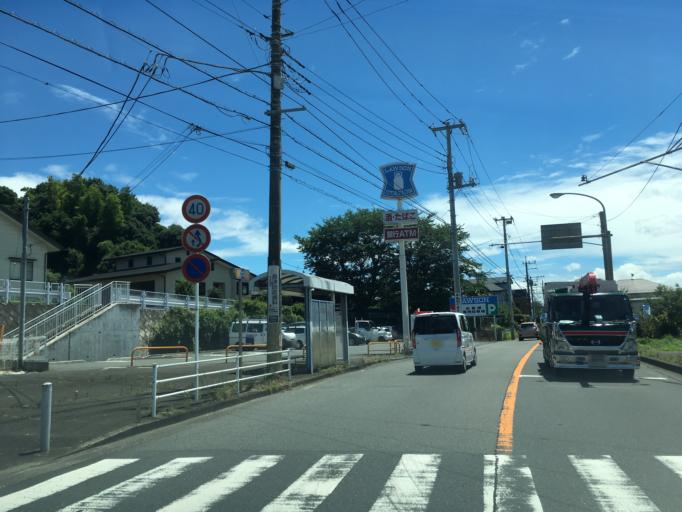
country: JP
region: Tokyo
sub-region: Machida-shi
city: Machida
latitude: 35.5425
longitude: 139.4966
